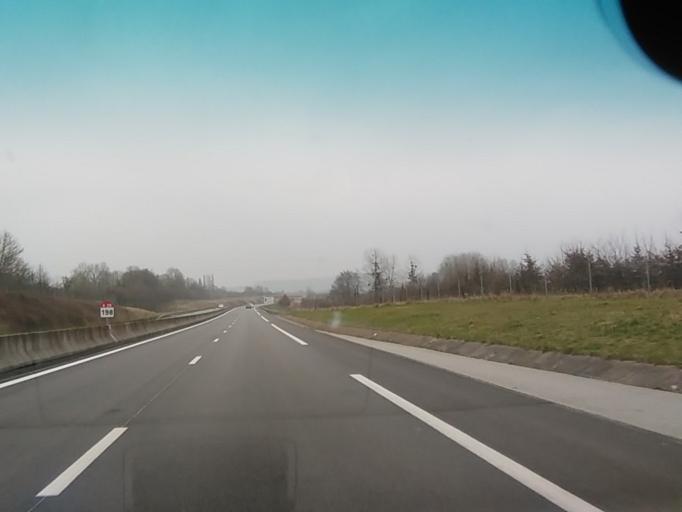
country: FR
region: Lower Normandy
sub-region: Departement de l'Orne
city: Gace
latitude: 48.7580
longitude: 0.2813
